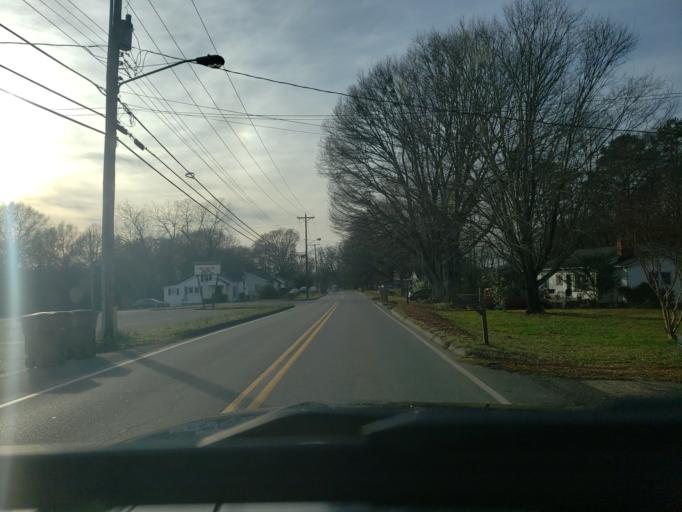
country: US
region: North Carolina
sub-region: Cleveland County
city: Shelby
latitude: 35.2800
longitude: -81.5176
